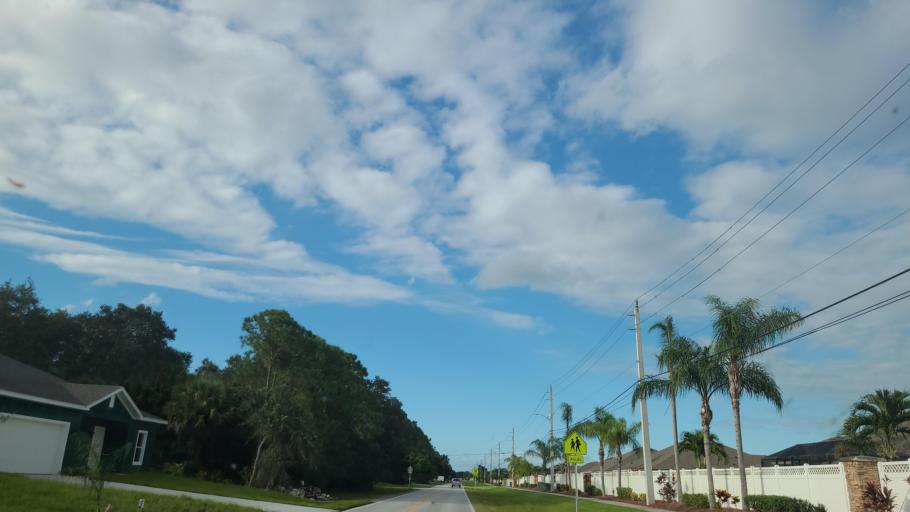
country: US
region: Florida
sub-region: Brevard County
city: June Park
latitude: 27.9898
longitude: -80.6882
